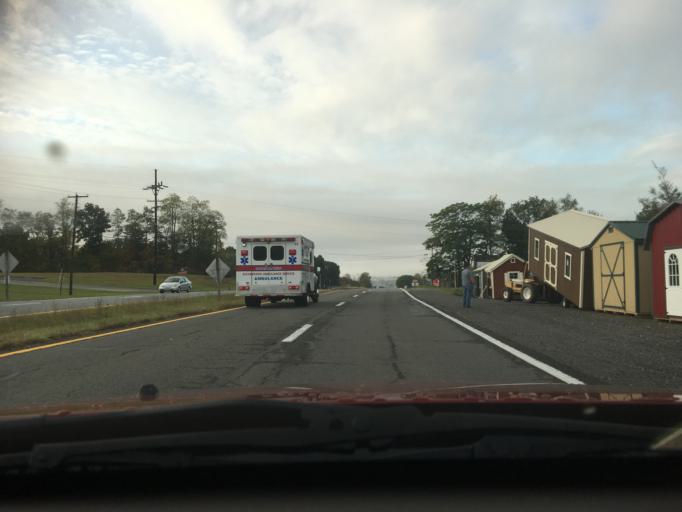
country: US
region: Virginia
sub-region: Pulaski County
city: Dublin
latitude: 37.0915
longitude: -80.6879
